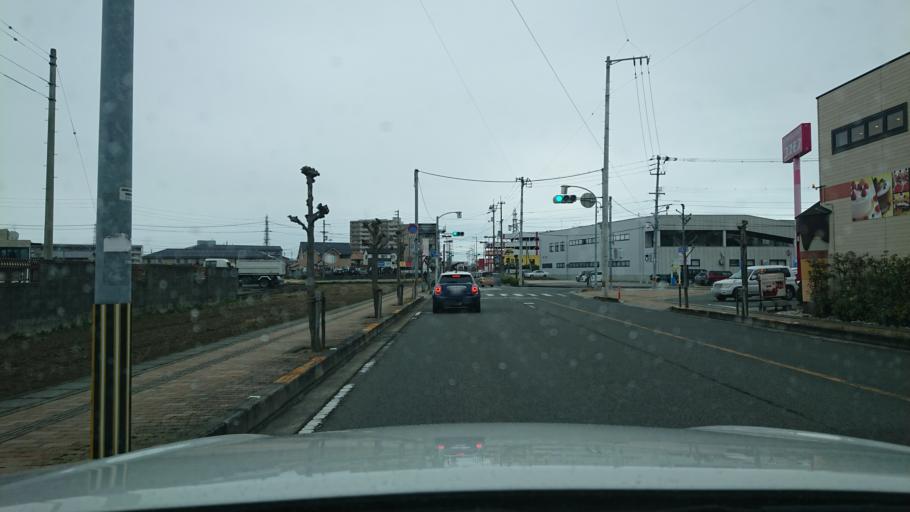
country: JP
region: Tokushima
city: Tokushima-shi
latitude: 34.0837
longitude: 134.5377
